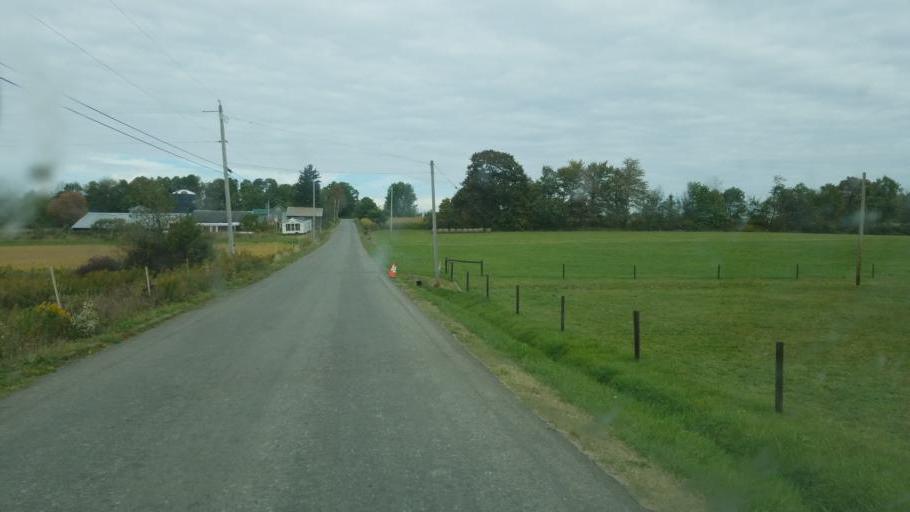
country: US
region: Pennsylvania
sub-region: Mercer County
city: Stoneboro
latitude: 41.3861
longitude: -80.2441
